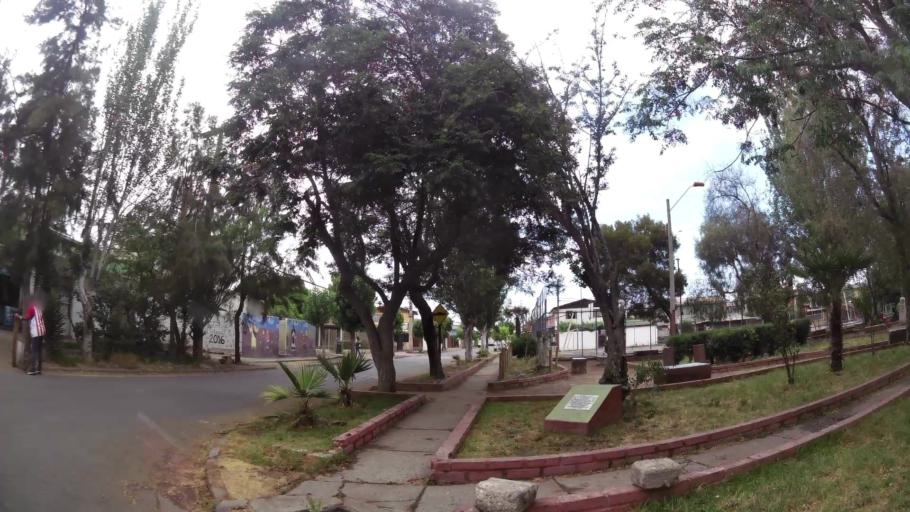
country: CL
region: Santiago Metropolitan
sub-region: Provincia de Santiago
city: Santiago
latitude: -33.5021
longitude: -70.6847
